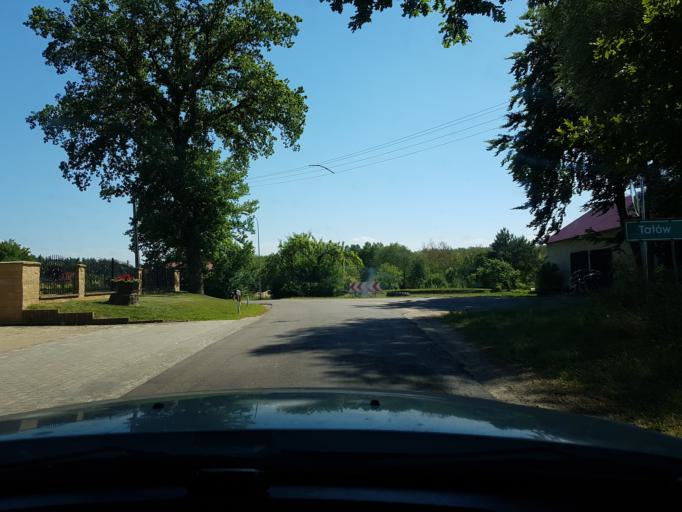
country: PL
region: West Pomeranian Voivodeship
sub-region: Powiat koszalinski
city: Mielno
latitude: 54.1744
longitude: 16.0789
